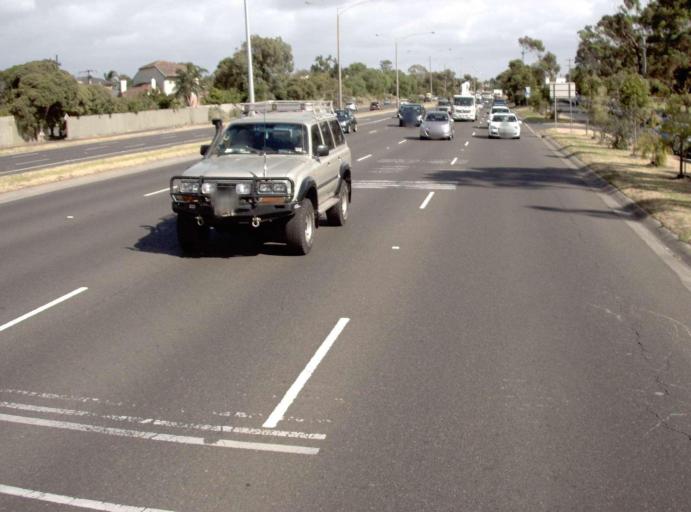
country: AU
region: Victoria
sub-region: Bayside
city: North Brighton
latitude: -37.9114
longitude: 145.0137
